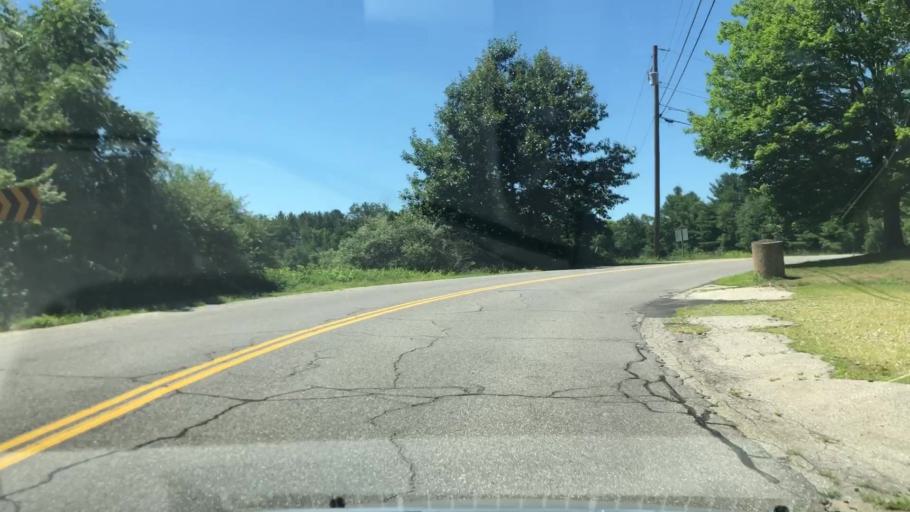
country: US
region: New Hampshire
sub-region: Hillsborough County
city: Milford
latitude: 42.8303
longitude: -71.5846
